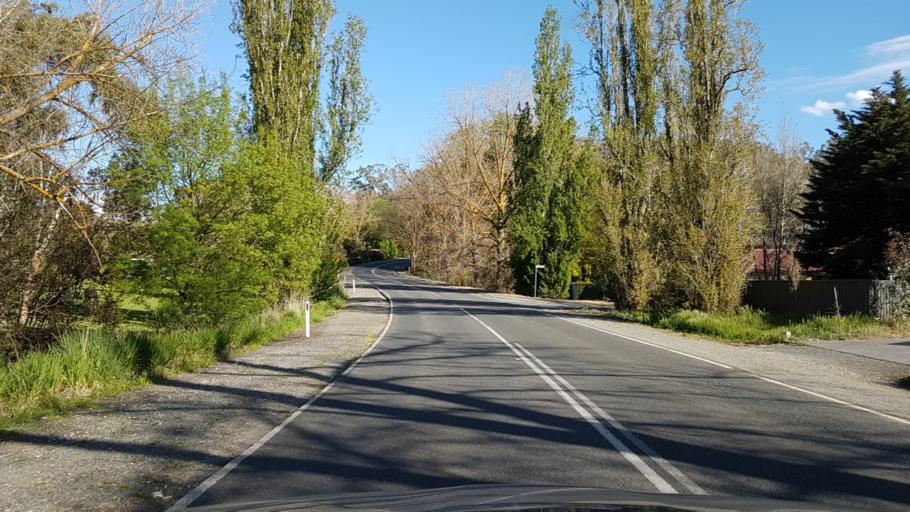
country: AU
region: South Australia
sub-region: Adelaide Hills
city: Gumeracha
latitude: -34.8273
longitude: 138.8873
